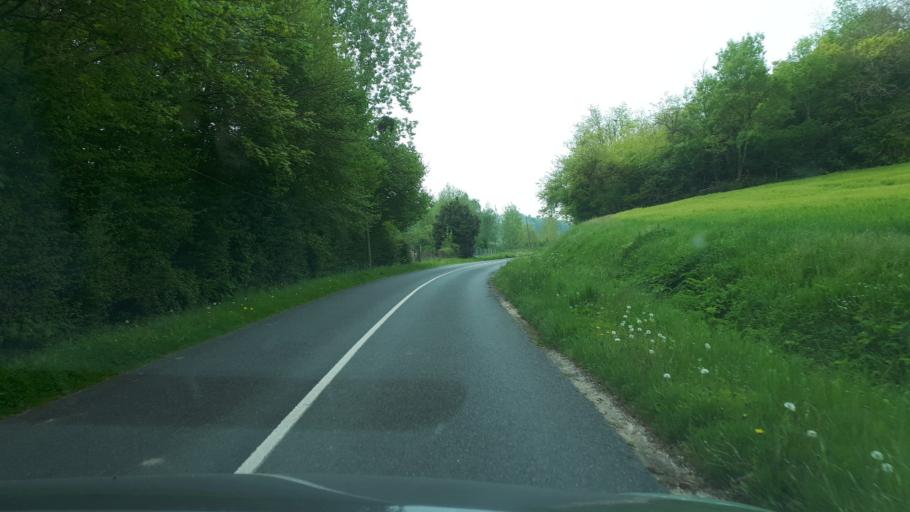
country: FR
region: Centre
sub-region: Departement du Loir-et-Cher
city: Lunay
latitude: 47.8156
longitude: 0.9551
